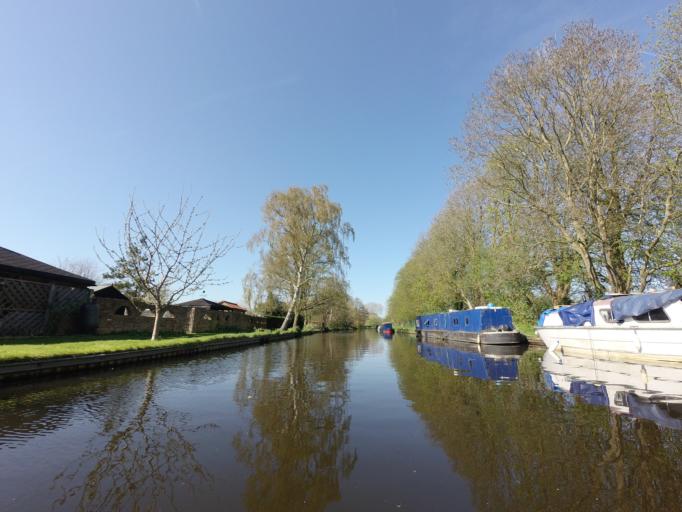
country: GB
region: England
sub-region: Greater London
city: Uxbridge
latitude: 51.5561
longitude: -0.4836
